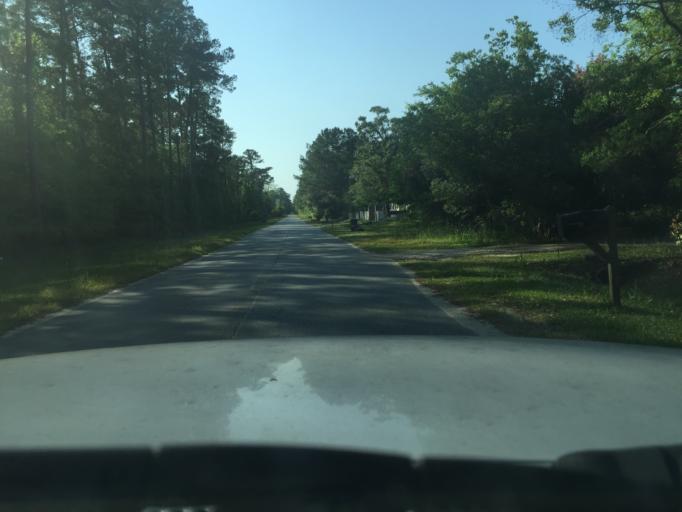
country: US
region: Georgia
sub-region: Chatham County
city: Georgetown
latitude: 32.0343
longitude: -81.2140
